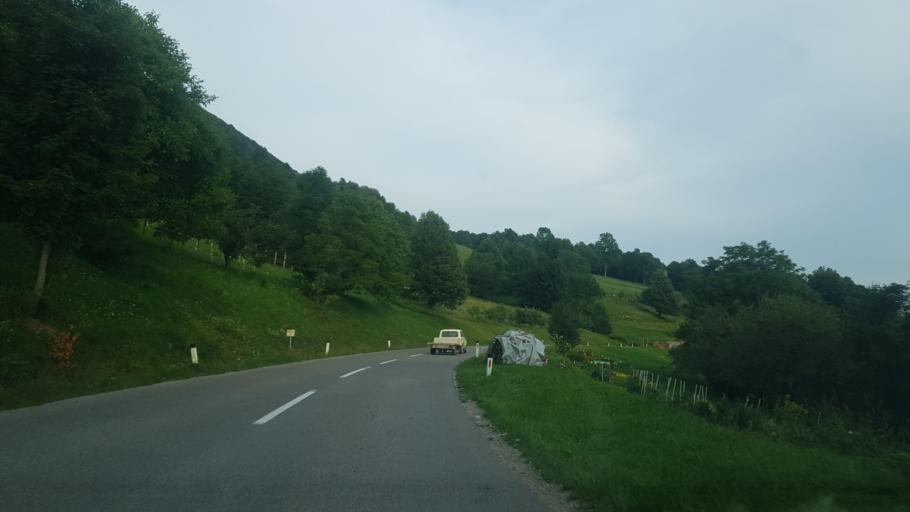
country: SI
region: Vipava
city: Vipava
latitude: 45.8673
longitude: 14.0579
